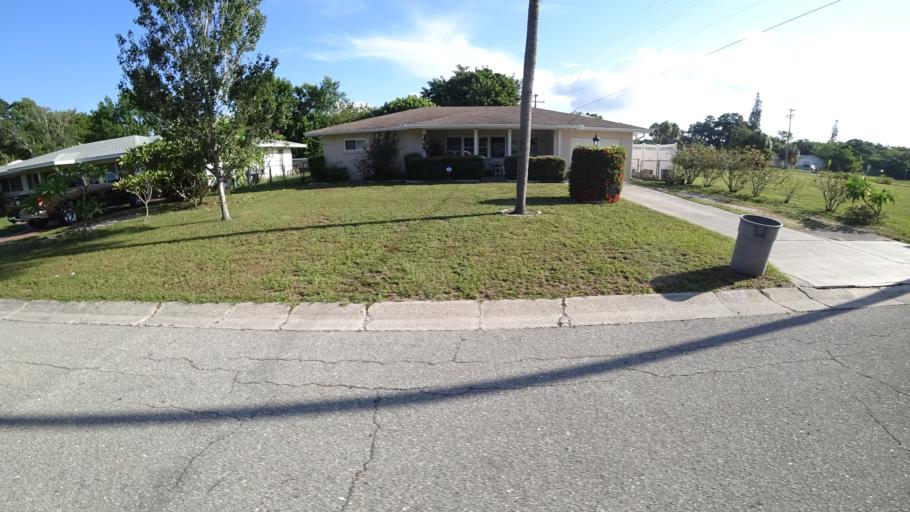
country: US
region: Florida
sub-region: Manatee County
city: South Bradenton
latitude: 27.4767
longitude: -82.5884
